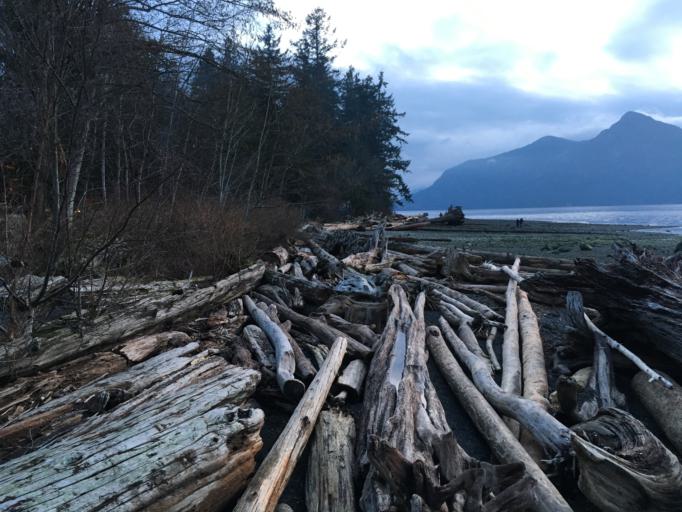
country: CA
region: British Columbia
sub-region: Greater Vancouver Regional District
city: Lions Bay
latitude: 49.5584
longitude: -123.2354
